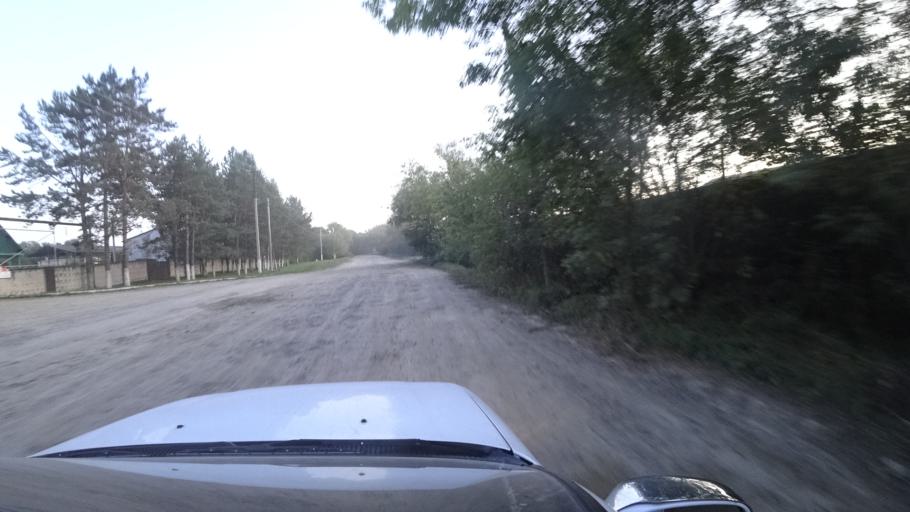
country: RU
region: Primorskiy
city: Dal'nerechensk
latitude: 45.9361
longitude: 133.7595
